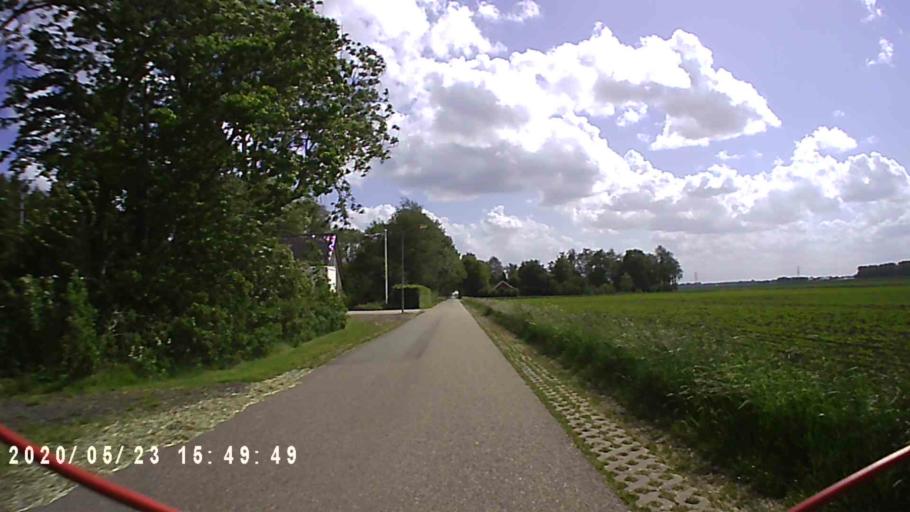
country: NL
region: Groningen
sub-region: Gemeente Delfzijl
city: Delfzijl
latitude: 53.2764
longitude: 6.9053
